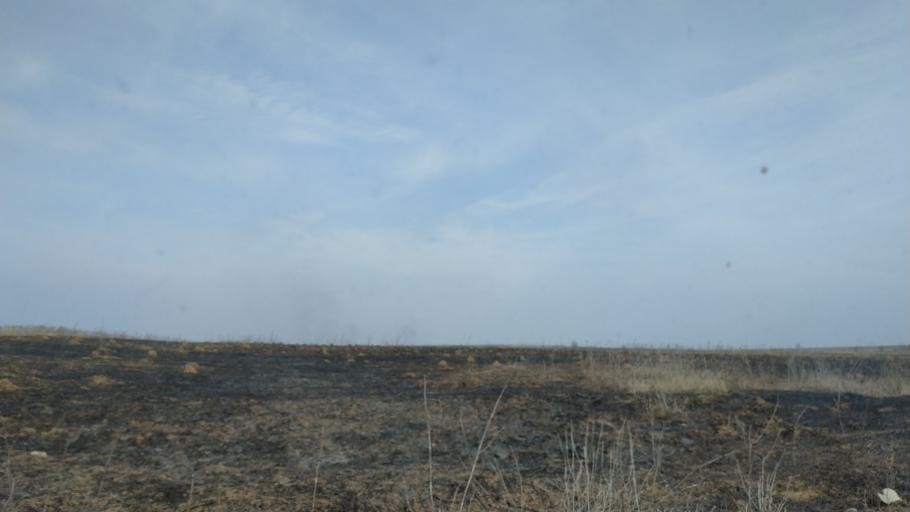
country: RU
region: Moskovskaya
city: Troitskoye
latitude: 55.3599
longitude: 38.4567
